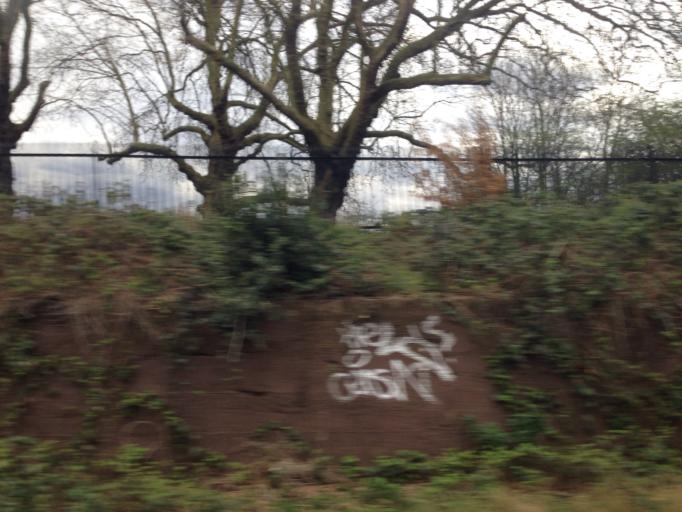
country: GB
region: England
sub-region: Greater London
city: Earlsfield
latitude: 51.4519
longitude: -0.1690
